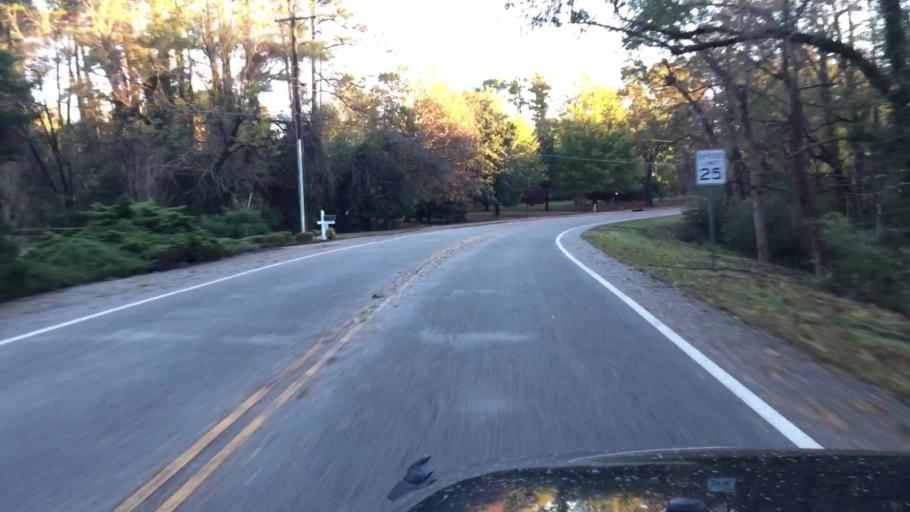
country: US
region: Virginia
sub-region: City of Williamsburg
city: Williamsburg
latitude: 37.2593
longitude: -76.7100
